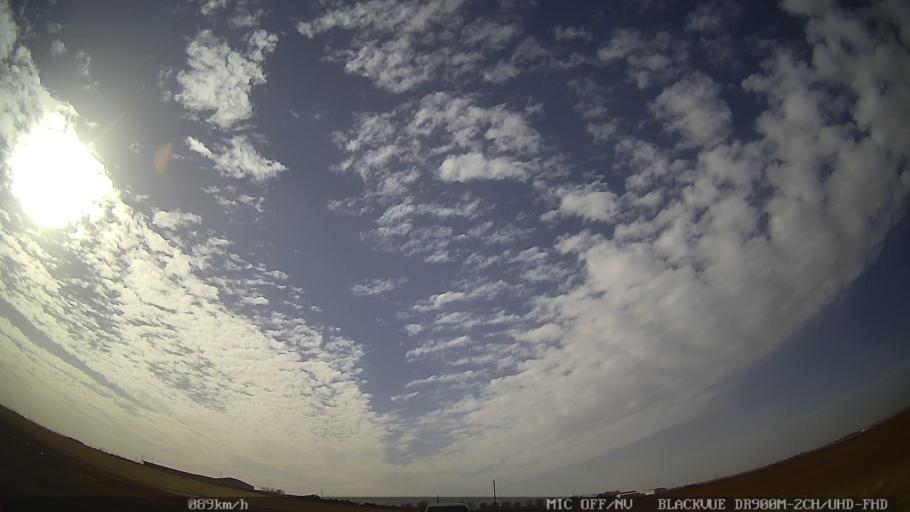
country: US
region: New Mexico
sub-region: Curry County
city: Clovis
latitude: 34.4192
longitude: -103.1299
